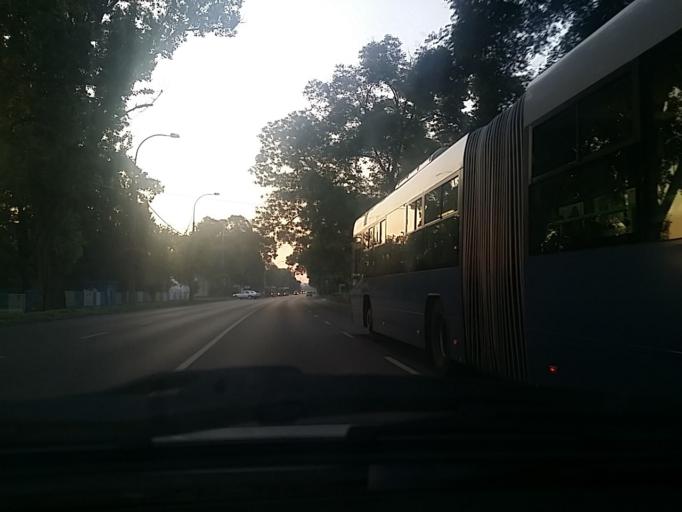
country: HU
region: Budapest
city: Budapest XVII. keruelet
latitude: 47.4816
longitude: 19.2471
